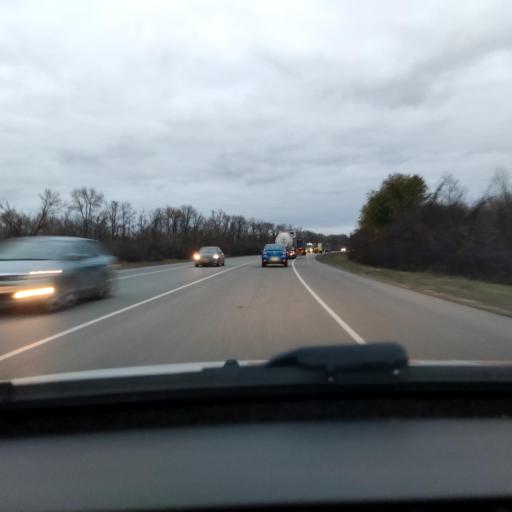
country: RU
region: Lipetsk
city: Borinskoye
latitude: 52.4550
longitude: 39.3020
